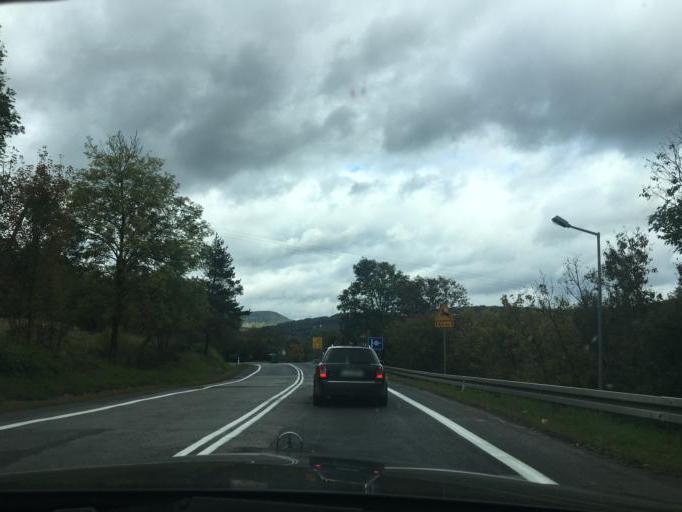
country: PL
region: Subcarpathian Voivodeship
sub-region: Powiat krosnienski
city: Dukla
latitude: 49.4733
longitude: 21.7080
